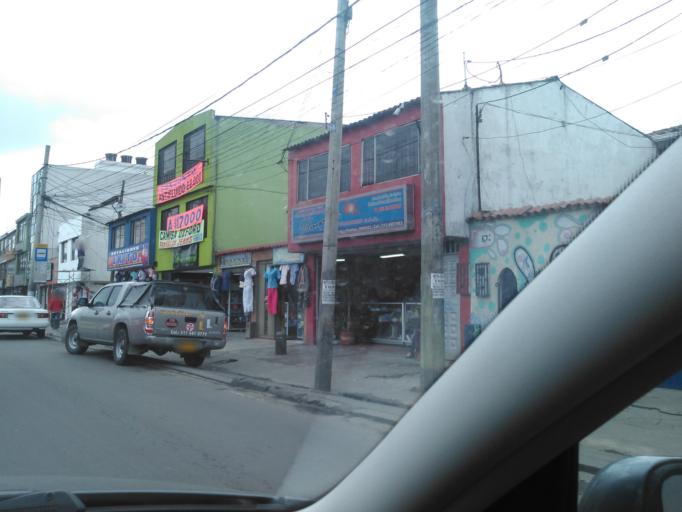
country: CO
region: Bogota D.C.
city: Bogota
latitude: 4.6107
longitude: -74.1285
